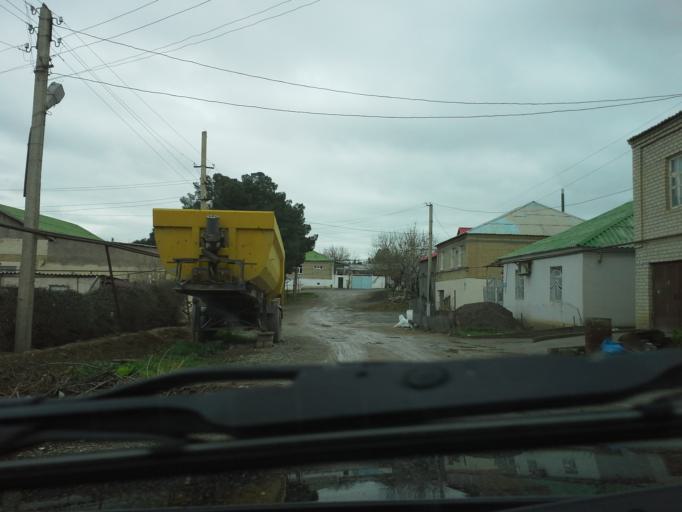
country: TM
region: Ahal
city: Abadan
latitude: 37.9592
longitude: 58.2175
